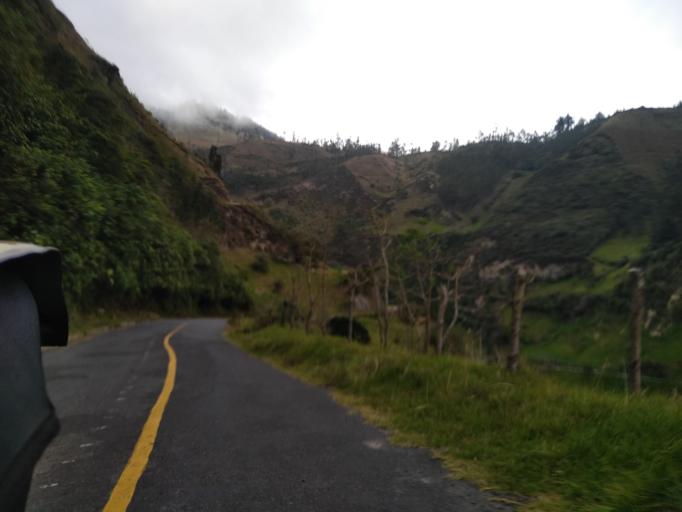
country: EC
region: Cotopaxi
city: Saquisili
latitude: -0.6908
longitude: -78.8687
